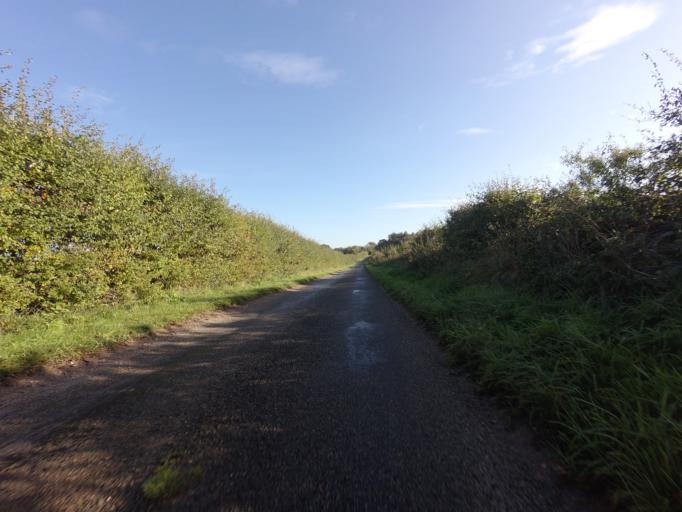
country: GB
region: England
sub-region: Norfolk
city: Dersingham
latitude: 52.8288
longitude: 0.5609
